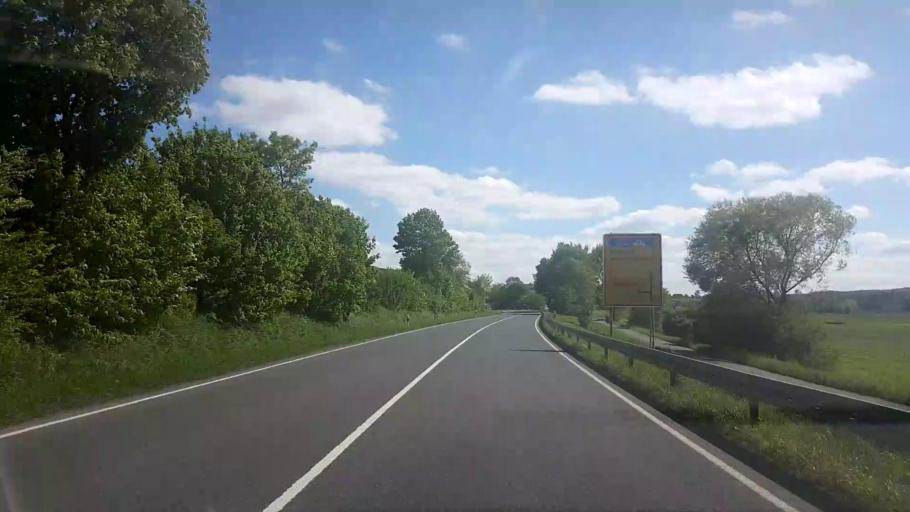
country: DE
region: Bavaria
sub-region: Regierungsbezirk Unterfranken
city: Untermerzbach
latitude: 50.0895
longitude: 10.8633
